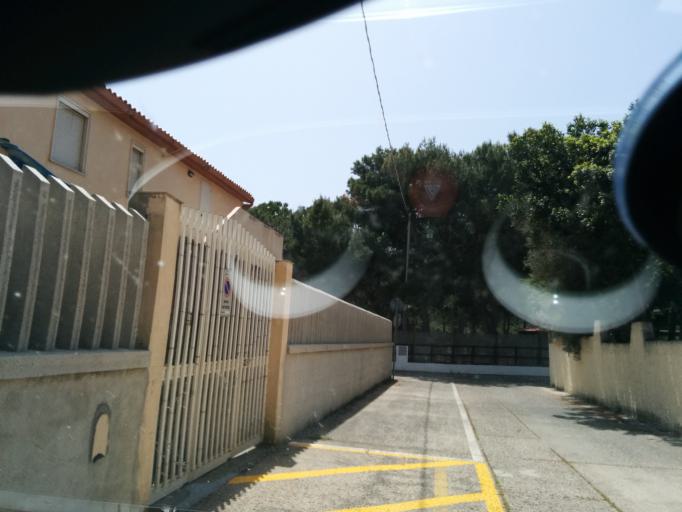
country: IT
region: Sardinia
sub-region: Provincia di Carbonia-Iglesias
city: Sant'Antioco
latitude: 38.9987
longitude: 8.4478
